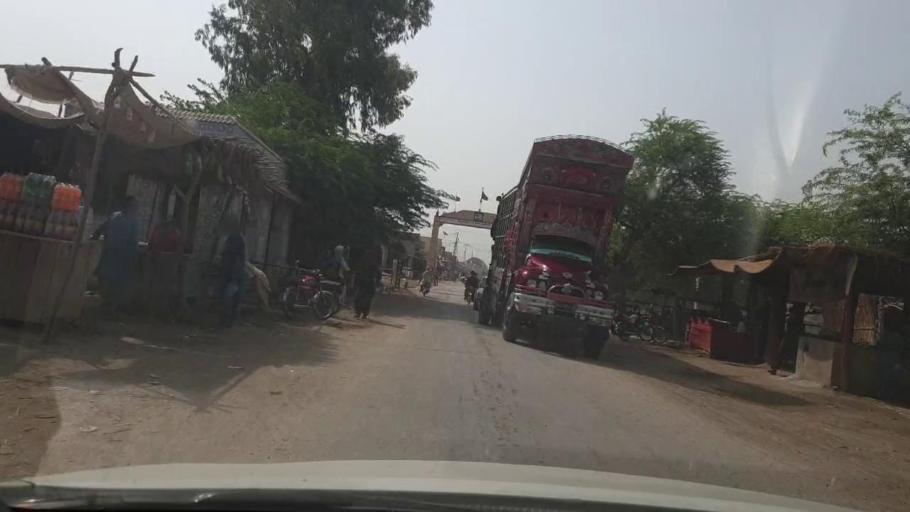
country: PK
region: Sindh
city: Kot Diji
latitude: 27.4324
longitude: 68.6512
